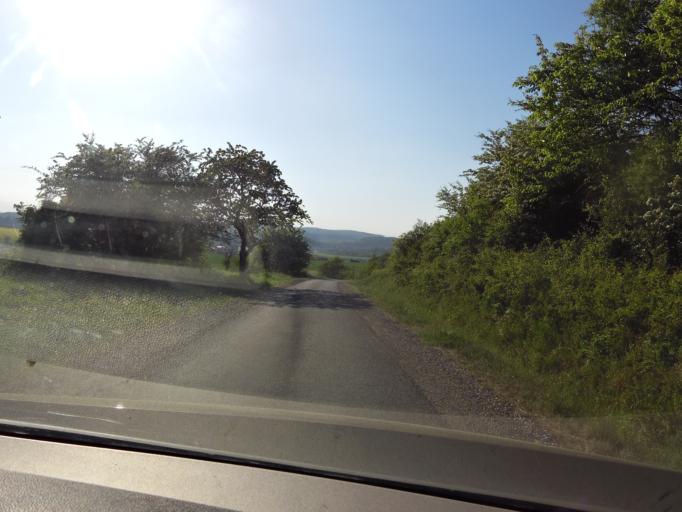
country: DE
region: Thuringia
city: Lauterbach
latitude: 51.0751
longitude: 10.3652
